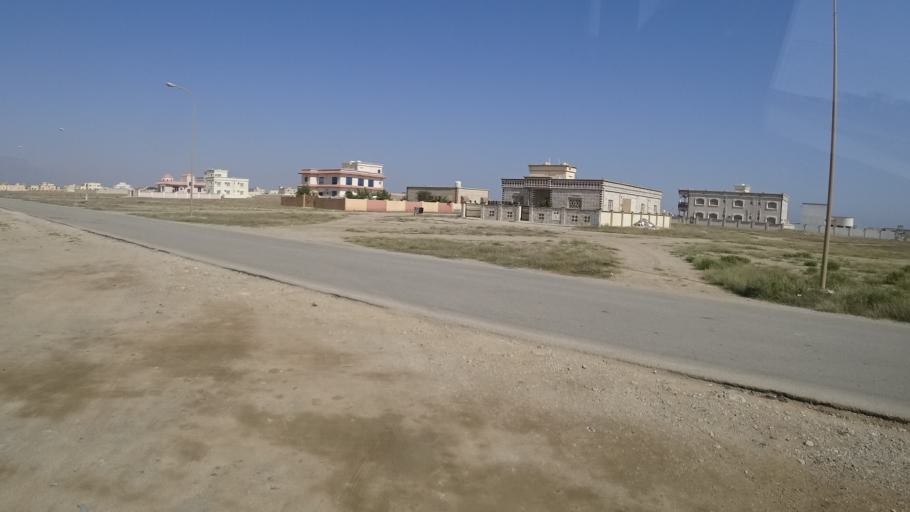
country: OM
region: Zufar
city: Salalah
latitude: 16.9822
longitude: 54.7106
